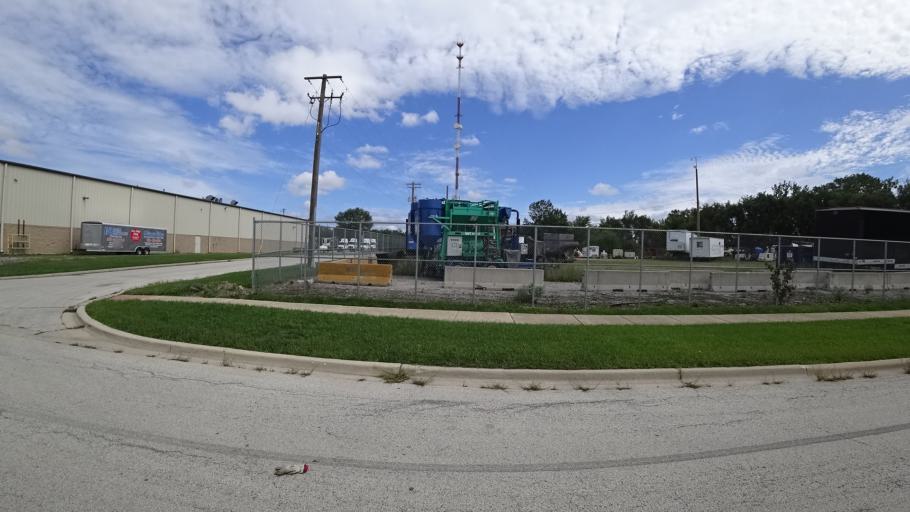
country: US
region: Illinois
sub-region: Cook County
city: Chicago Ridge
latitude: 41.7080
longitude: -87.7860
